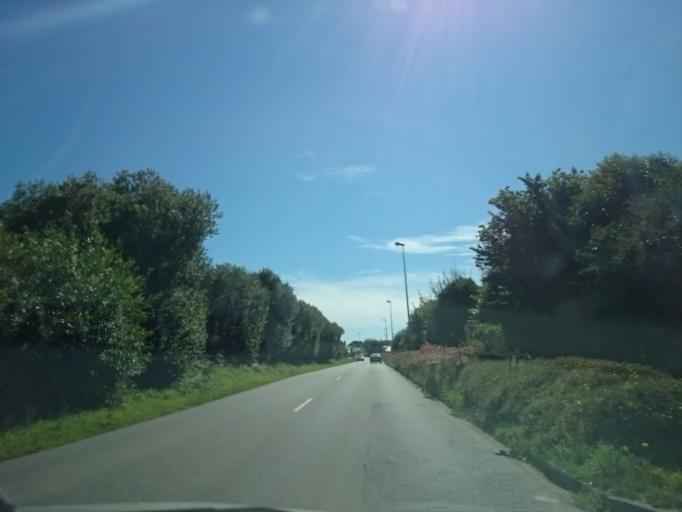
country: FR
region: Brittany
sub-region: Departement du Finistere
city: Saint-Renan
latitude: 48.4371
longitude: -4.6306
